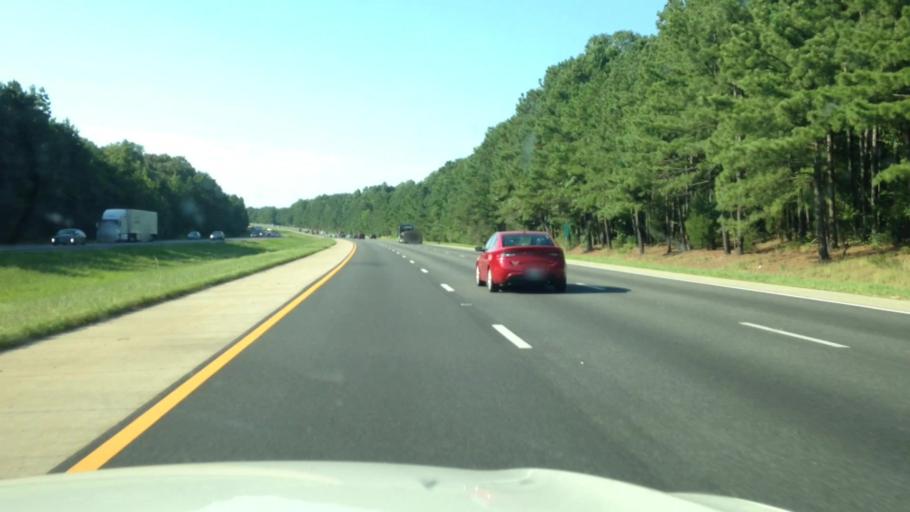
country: US
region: Virginia
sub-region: Chesterfield County
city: Enon
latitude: 37.4050
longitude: -77.3423
